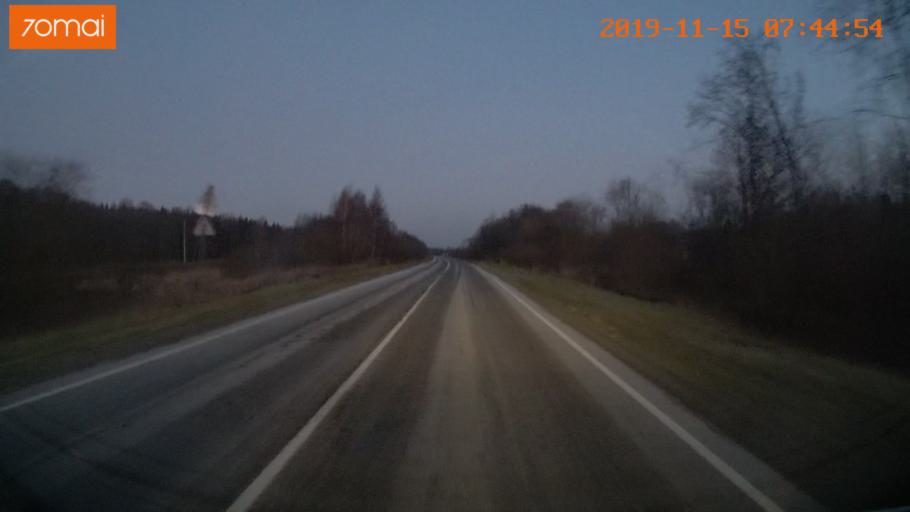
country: RU
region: Vologda
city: Sheksna
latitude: 58.8182
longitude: 38.3064
